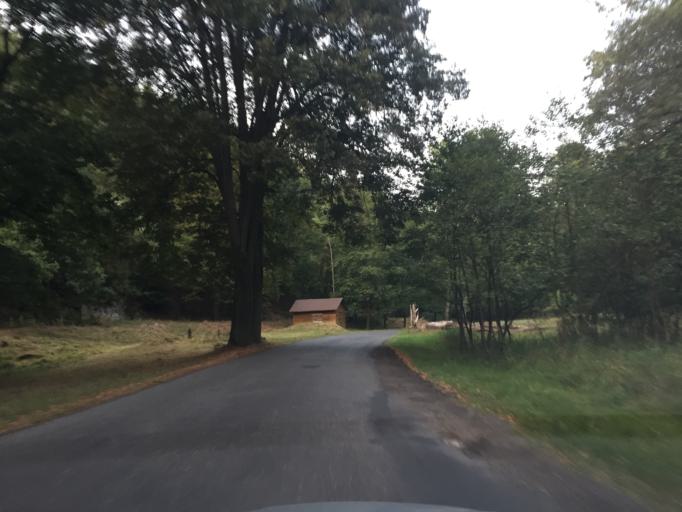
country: CZ
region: Ustecky
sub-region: Okres Decin
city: Chribska
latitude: 50.8588
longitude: 14.4369
